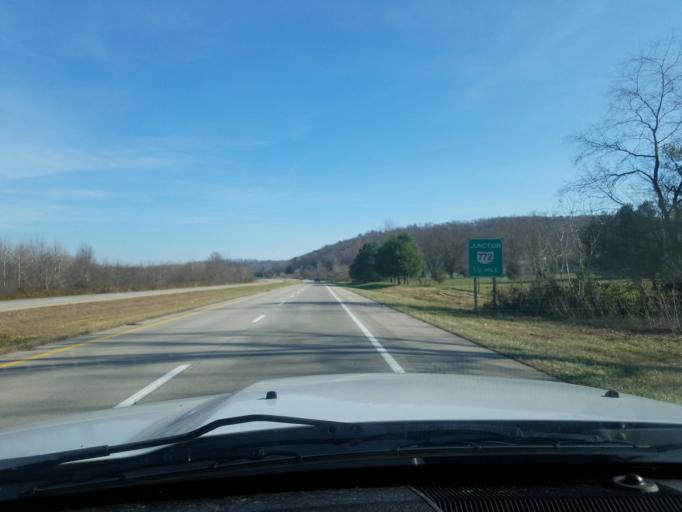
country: US
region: Ohio
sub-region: Pike County
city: Piketon
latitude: 39.0428
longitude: -83.1540
